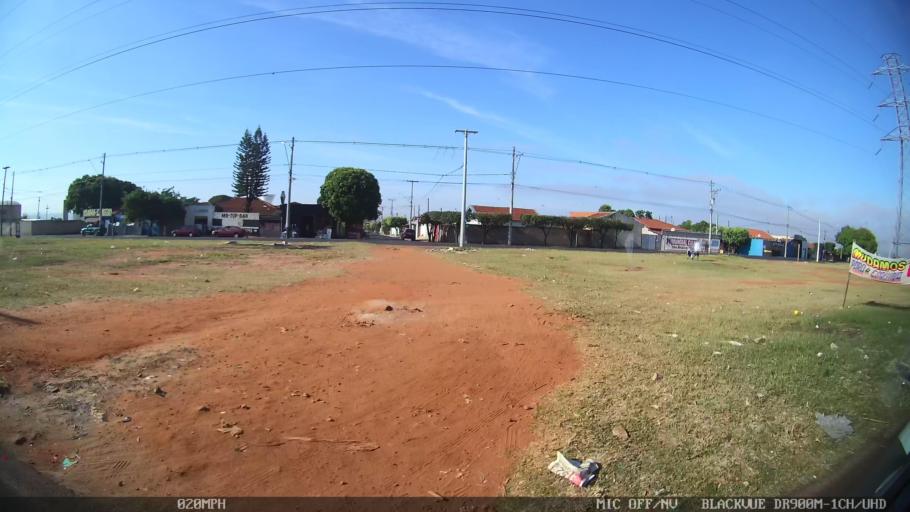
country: BR
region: Sao Paulo
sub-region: Sao Jose Do Rio Preto
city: Sao Jose do Rio Preto
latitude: -20.7809
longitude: -49.4057
